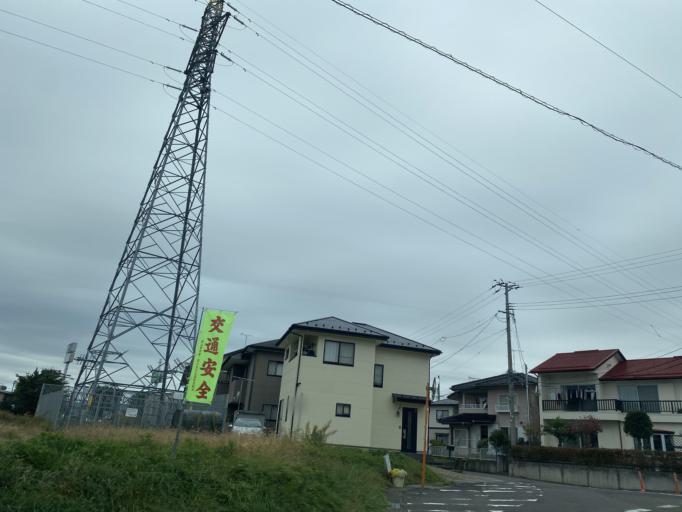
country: JP
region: Fukushima
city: Koriyama
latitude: 37.3725
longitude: 140.3509
